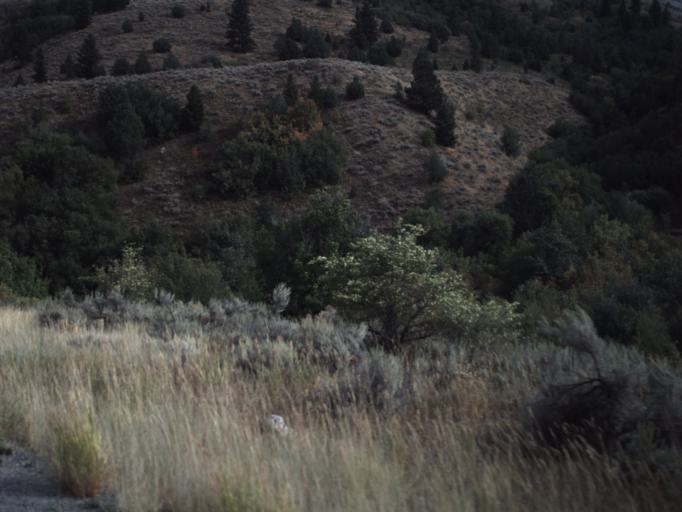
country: US
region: Utah
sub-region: Cache County
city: Millville
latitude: 41.6078
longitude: -111.6155
